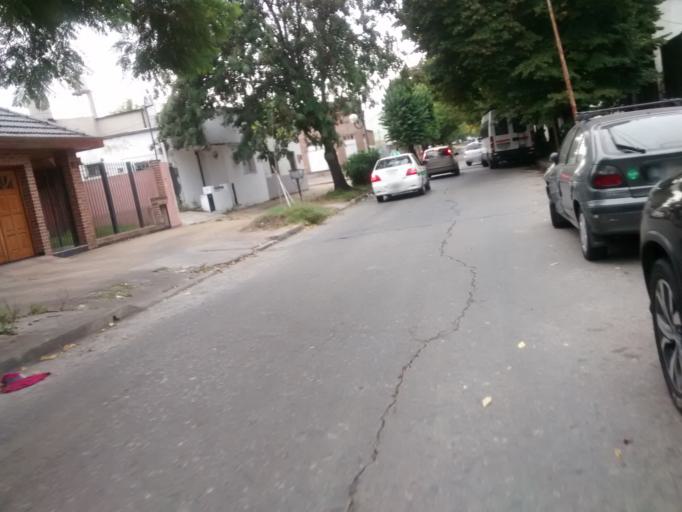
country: AR
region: Buenos Aires
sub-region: Partido de La Plata
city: La Plata
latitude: -34.9388
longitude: -57.9517
